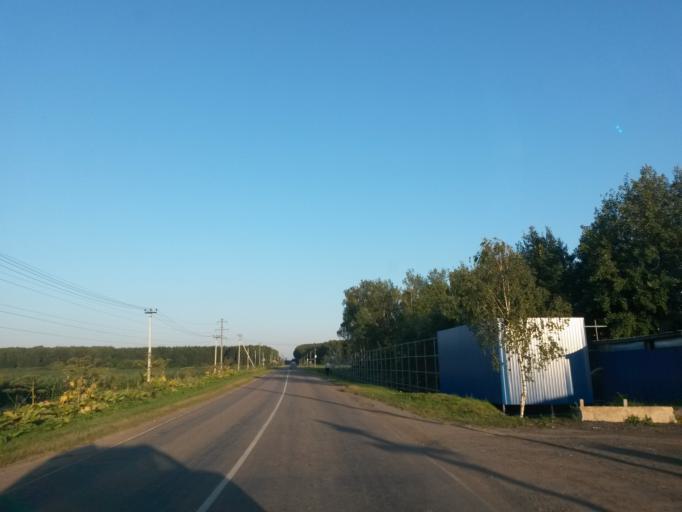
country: RU
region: Moskovskaya
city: Belyye Stolby
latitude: 55.2625
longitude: 37.7645
